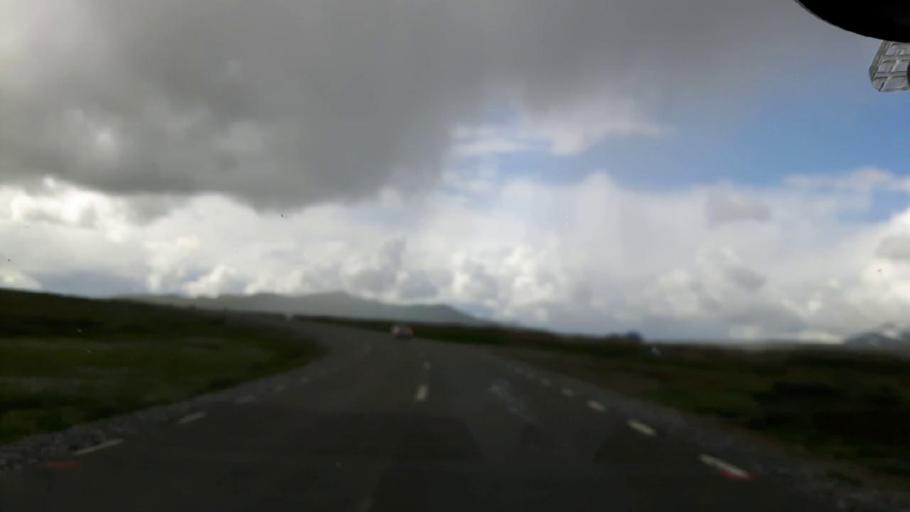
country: NO
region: Nordland
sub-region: Hattfjelldal
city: Hattfjelldal
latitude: 65.1031
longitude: 14.4694
